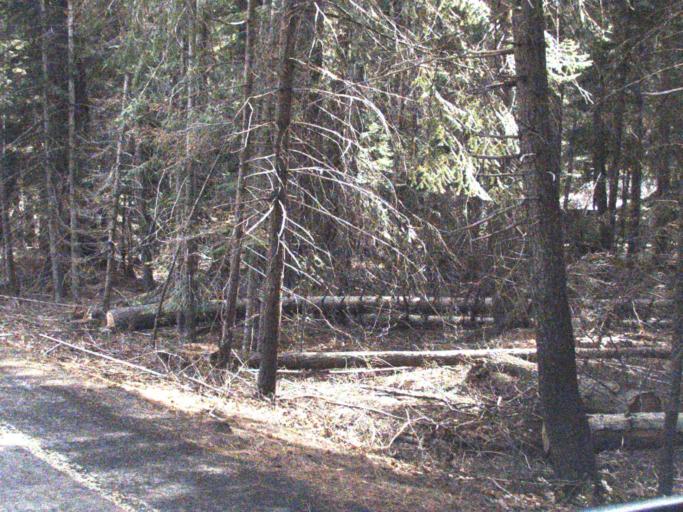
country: US
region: Washington
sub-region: Kittitas County
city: Cle Elum
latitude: 46.9813
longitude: -121.1318
